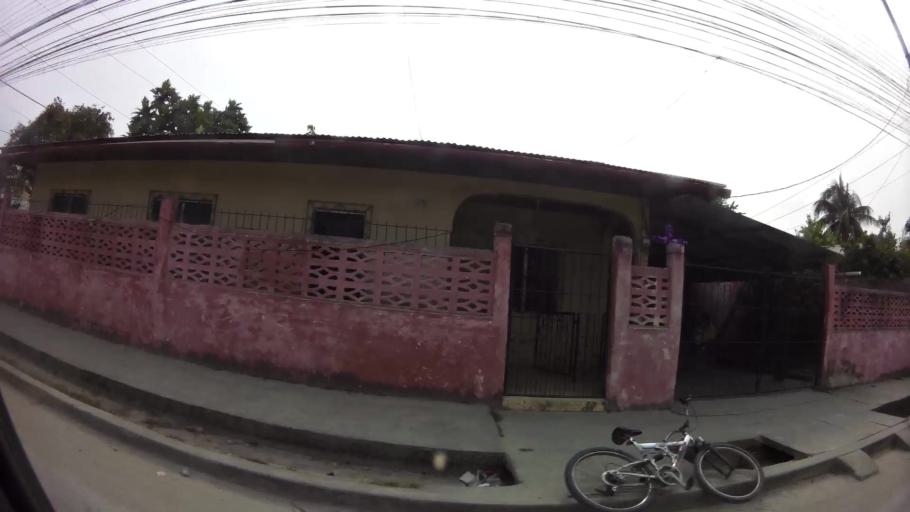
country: HN
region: Atlantida
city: Tela
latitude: 15.7784
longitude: -87.4512
